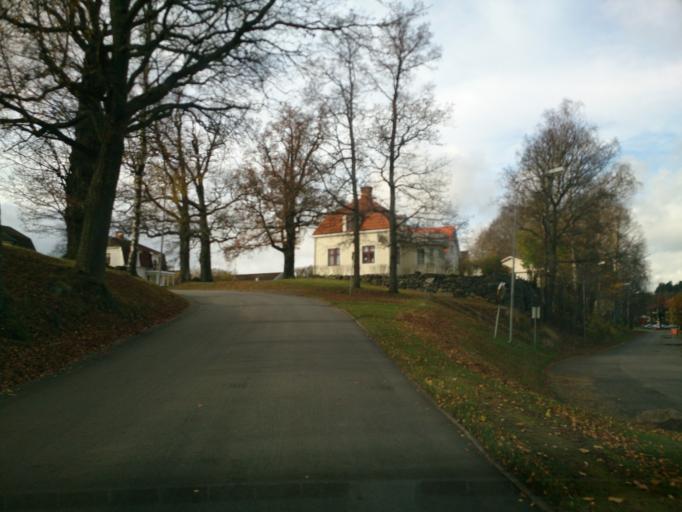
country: SE
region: OEstergoetland
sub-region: Atvidabergs Kommun
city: Atvidaberg
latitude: 58.2029
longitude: 15.9978
